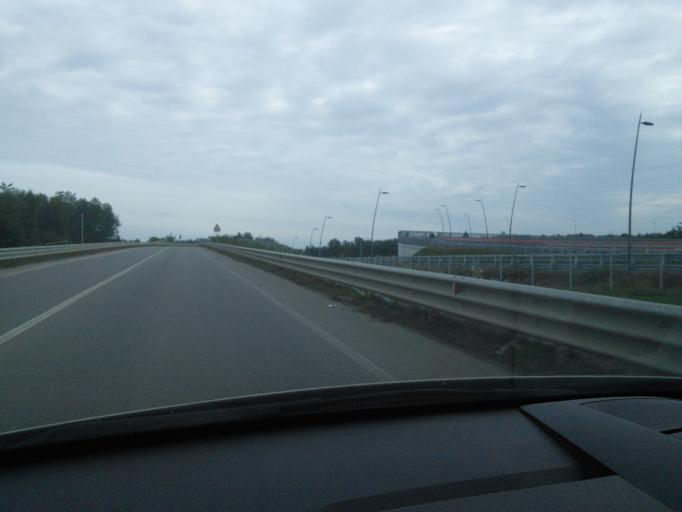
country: IT
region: Lombardy
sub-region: Provincia di Como
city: Cirimido
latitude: 45.6799
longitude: 9.0136
